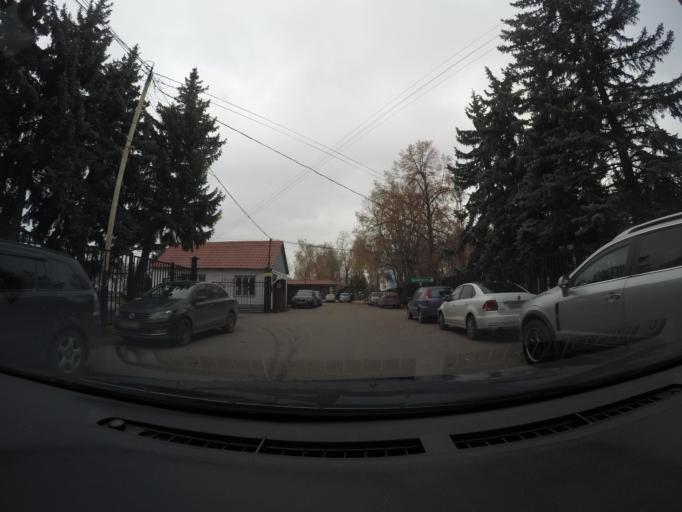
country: RU
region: Moscow
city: Ostankinskiy
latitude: 55.8178
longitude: 37.6135
